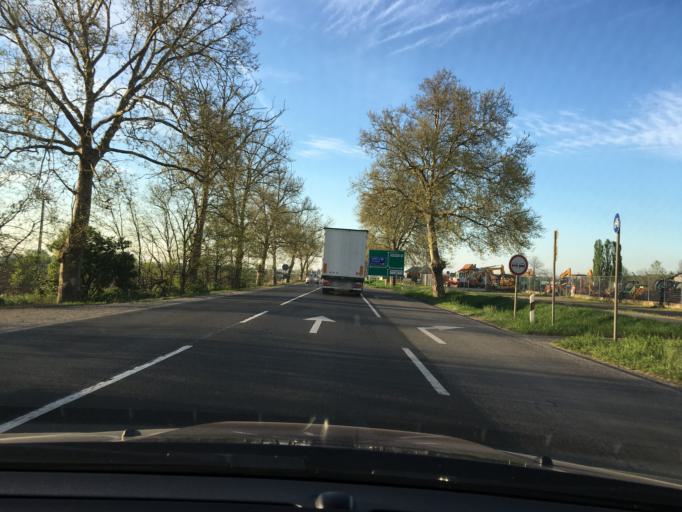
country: HU
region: Hajdu-Bihar
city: Mikepercs
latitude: 47.4593
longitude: 21.6367
